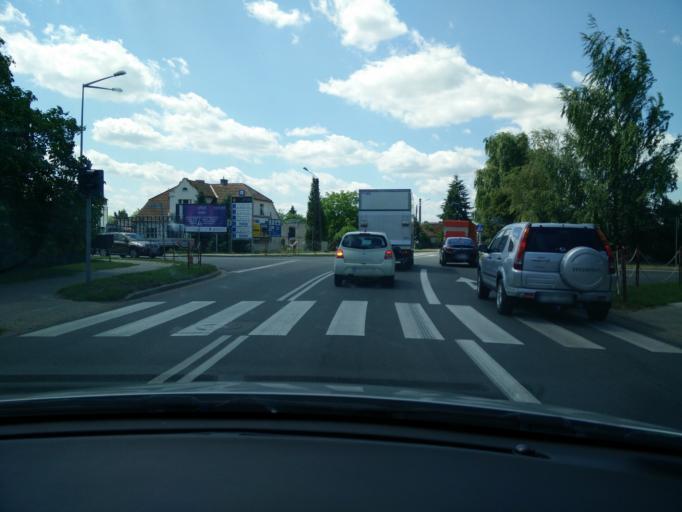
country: PL
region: Greater Poland Voivodeship
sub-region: Powiat sredzki
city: Sroda Wielkopolska
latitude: 52.2239
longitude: 17.2855
